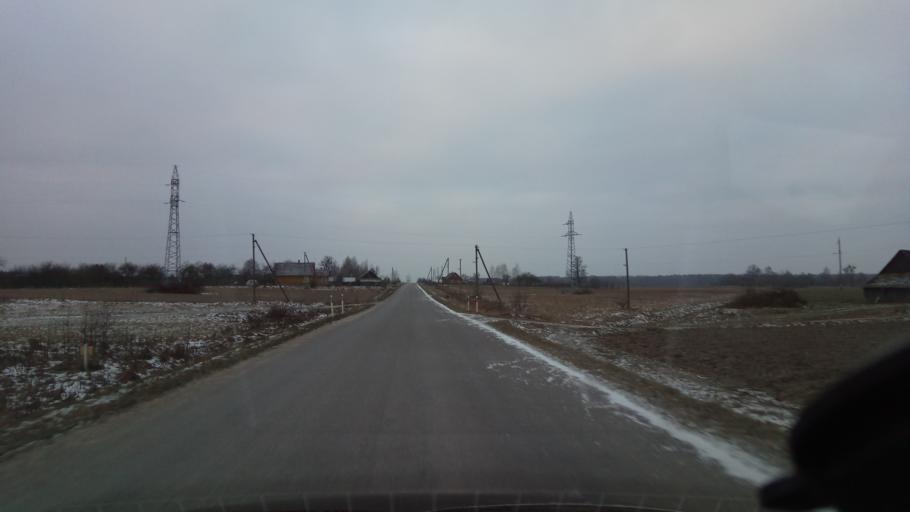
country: LT
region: Alytaus apskritis
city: Varena
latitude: 54.1169
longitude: 24.7490
